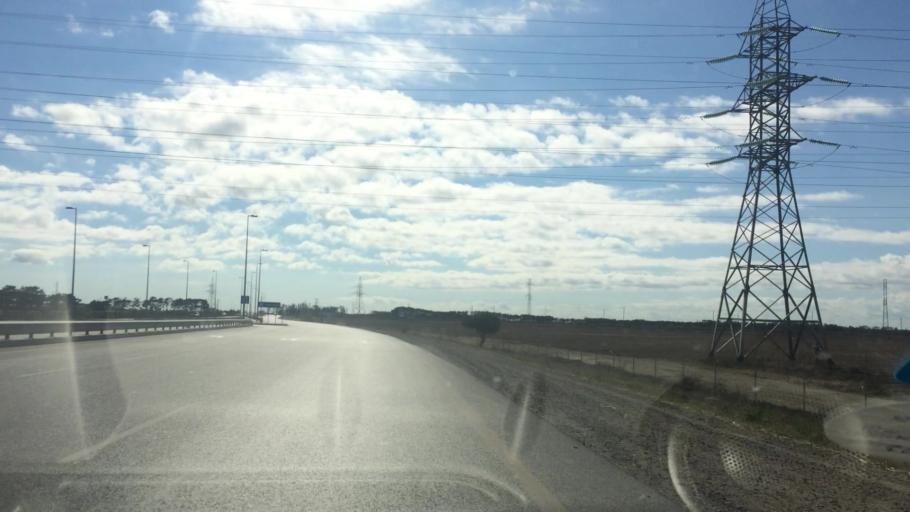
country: AZ
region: Baki
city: Qala
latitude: 40.4371
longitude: 50.1841
